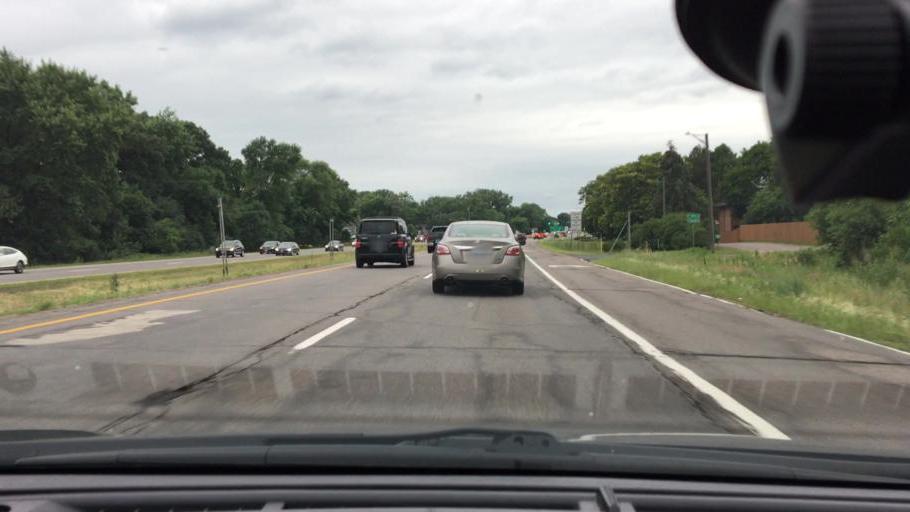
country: US
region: Minnesota
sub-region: Hennepin County
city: Golden Valley
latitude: 44.9833
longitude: -93.3728
